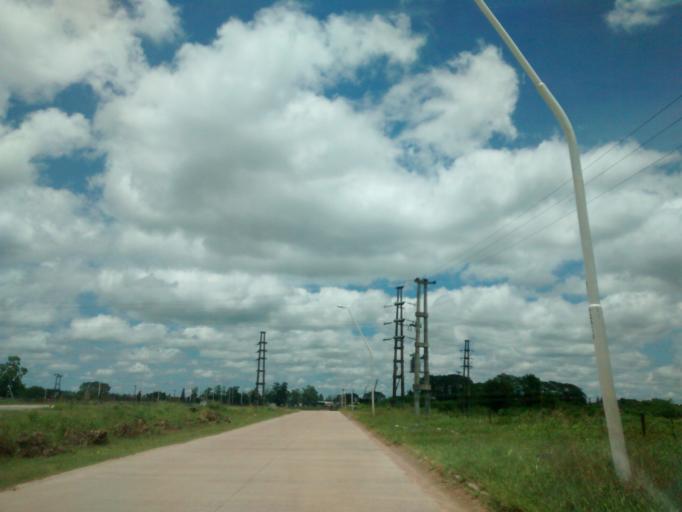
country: AR
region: Chaco
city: Fontana
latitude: -27.4092
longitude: -58.9891
